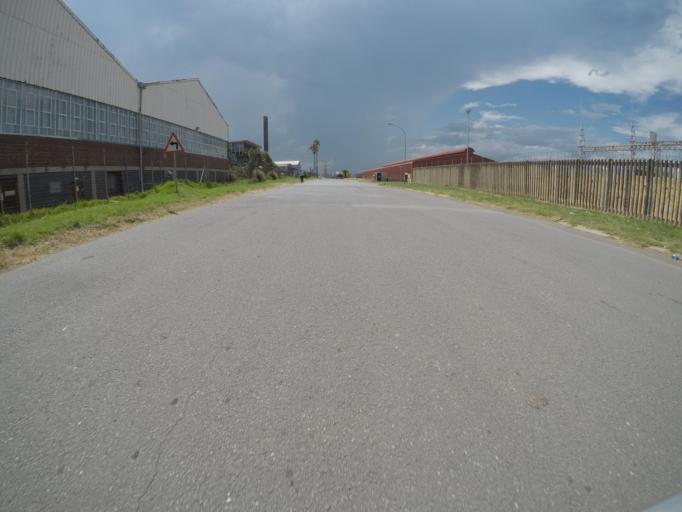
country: ZA
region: Eastern Cape
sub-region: Buffalo City Metropolitan Municipality
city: East London
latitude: -33.0305
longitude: 27.8793
